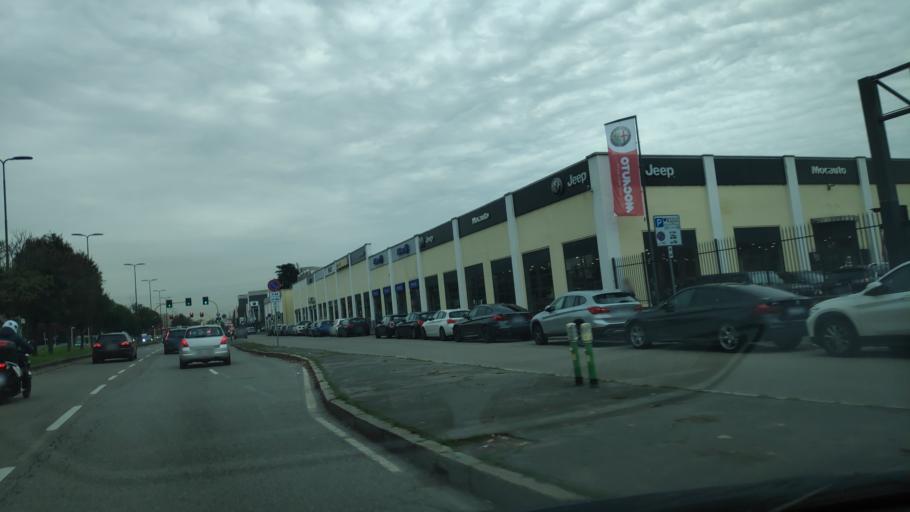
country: IT
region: Lombardy
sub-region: Citta metropolitana di Milano
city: Rozzano
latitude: 45.4123
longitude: 9.1749
